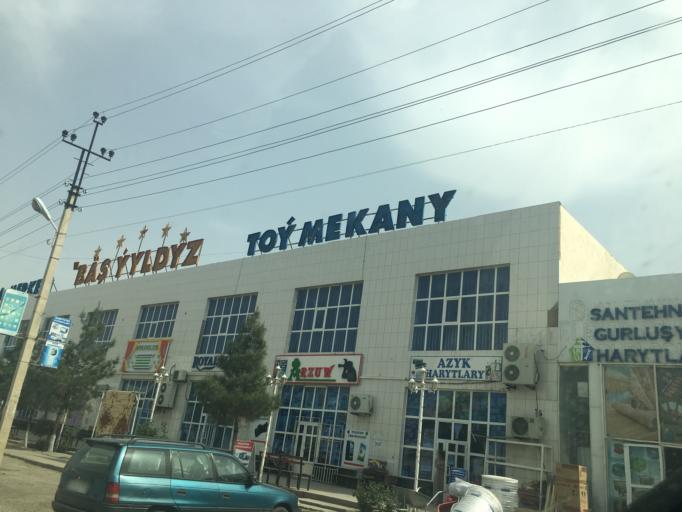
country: TM
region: Mary
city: Mary
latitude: 37.5961
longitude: 61.8611
